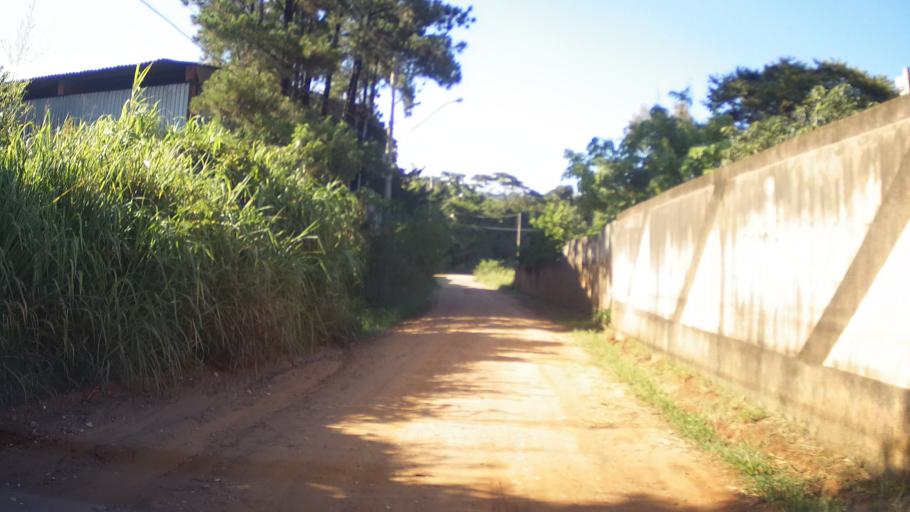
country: BR
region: Sao Paulo
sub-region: Itupeva
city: Itupeva
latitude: -23.1909
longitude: -46.9966
